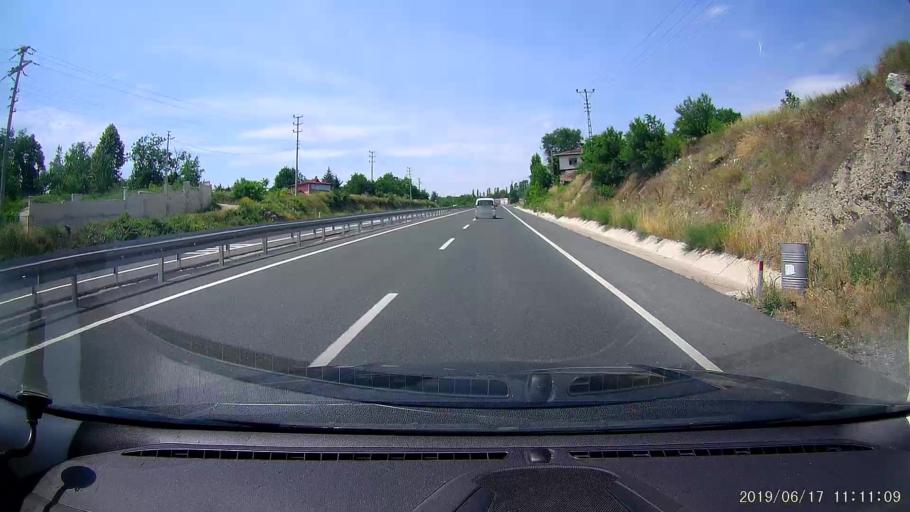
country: TR
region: Kastamonu
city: Tosya
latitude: 40.9903
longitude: 34.0132
